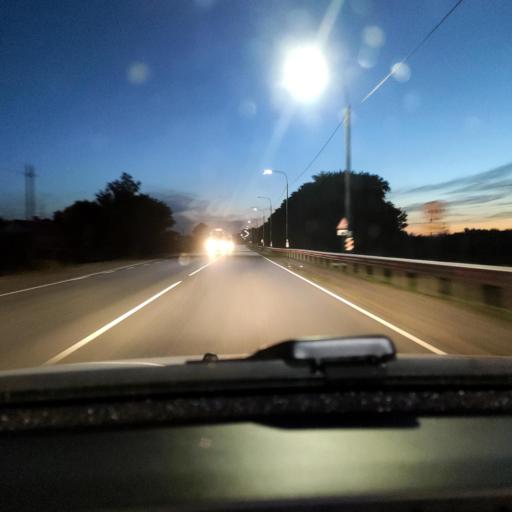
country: RU
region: Voronezj
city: Kashirskoye
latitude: 51.4584
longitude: 39.8060
